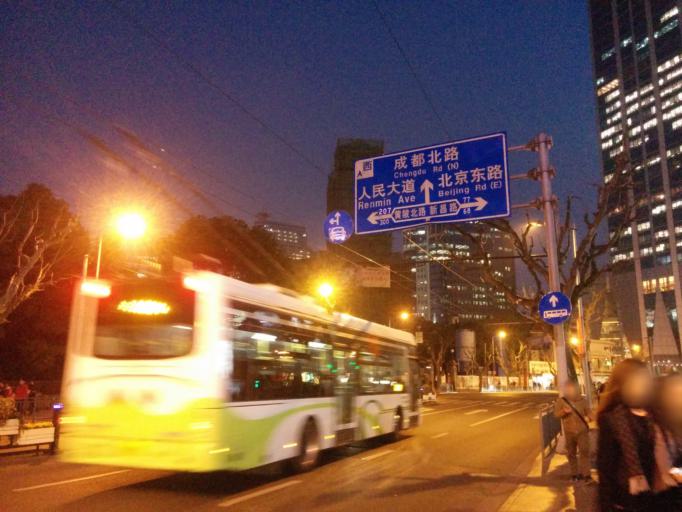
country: CN
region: Shanghai Shi
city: Shanghai
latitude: 31.2341
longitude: 121.4662
